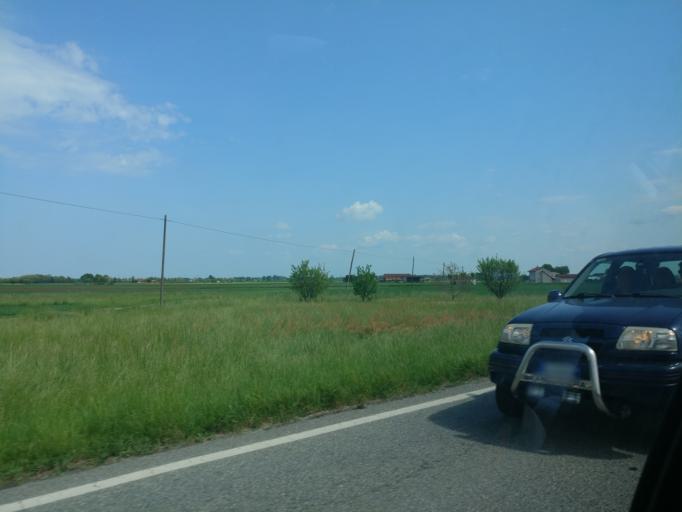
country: IT
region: Piedmont
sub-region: Provincia di Torino
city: Cavour
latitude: 44.7725
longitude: 7.3899
